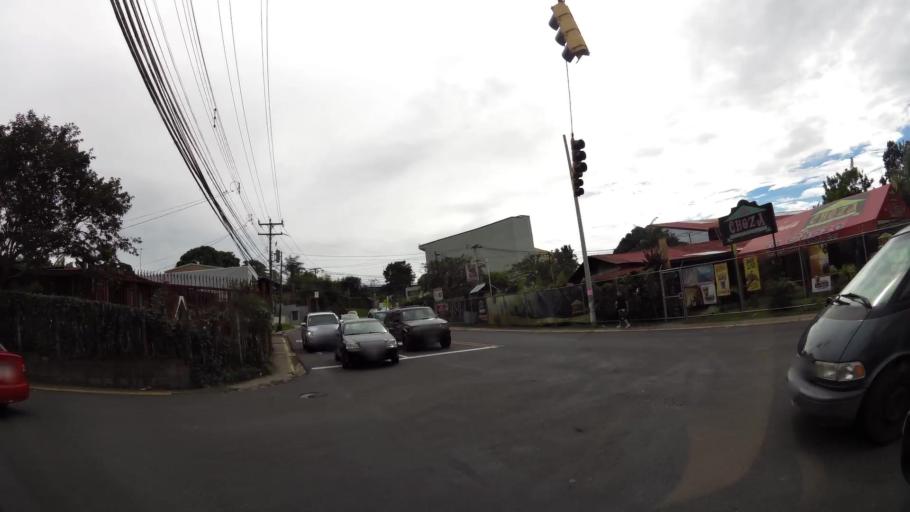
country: CR
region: San Jose
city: Sabanilla
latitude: 9.9454
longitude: -84.0324
